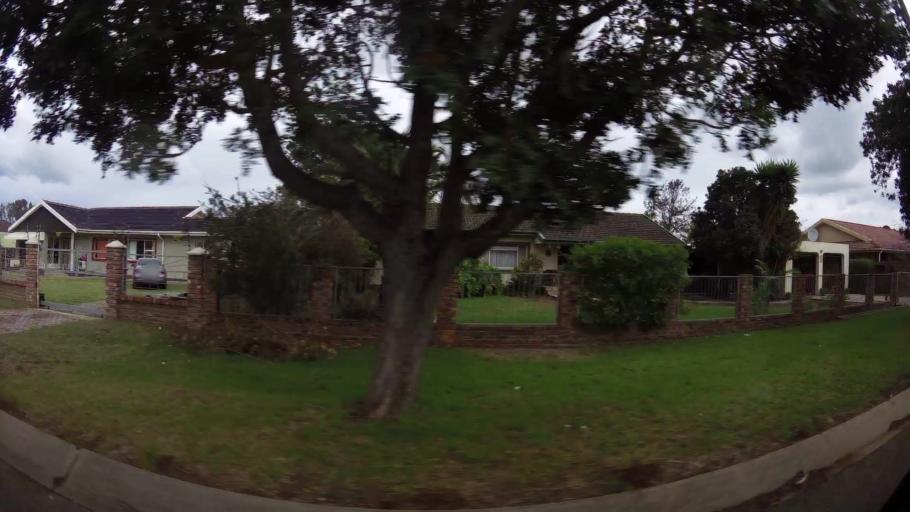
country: ZA
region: Eastern Cape
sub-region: Nelson Mandela Bay Metropolitan Municipality
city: Port Elizabeth
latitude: -33.9345
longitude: 25.5145
